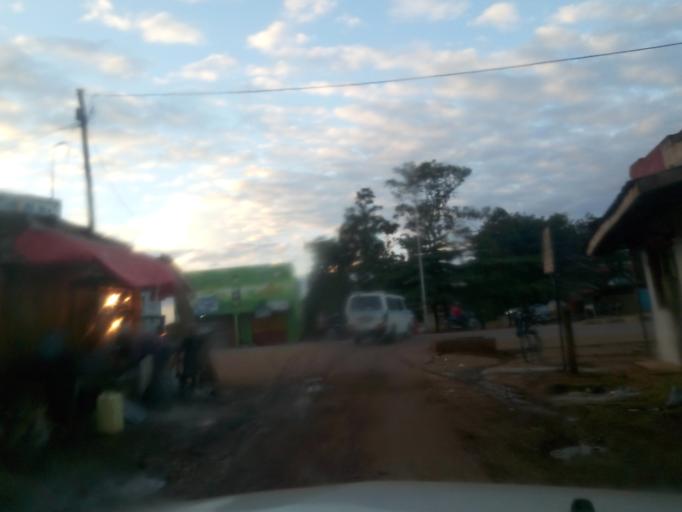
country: UG
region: Central Region
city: Kampala Central Division
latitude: 0.3820
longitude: 32.5649
